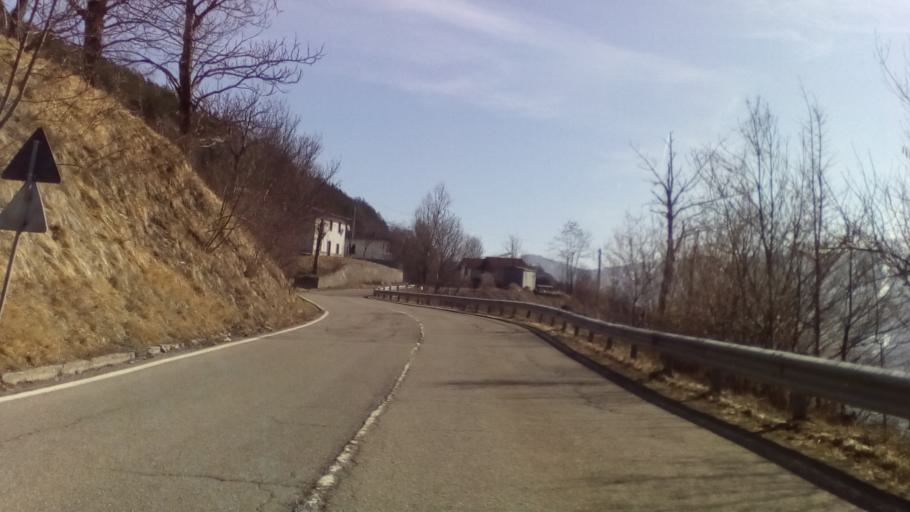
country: IT
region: Emilia-Romagna
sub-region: Provincia di Modena
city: Riolunato
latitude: 44.2581
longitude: 10.6432
